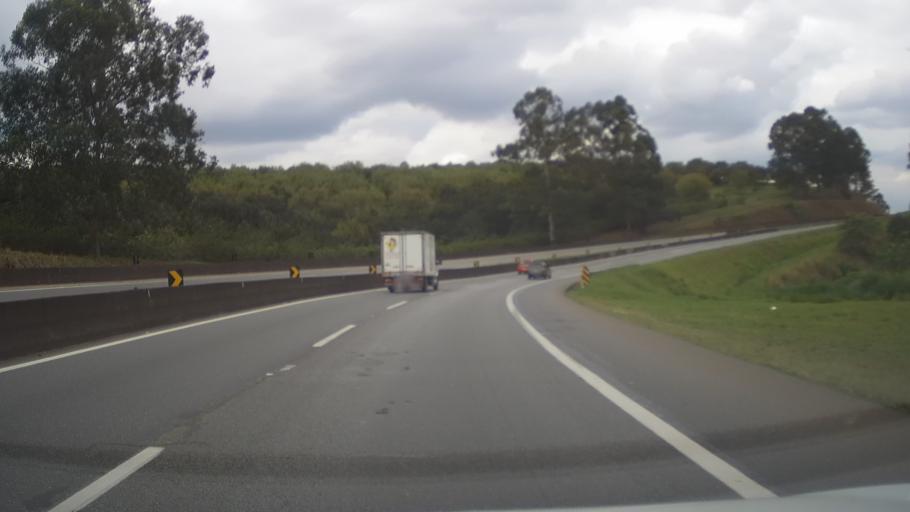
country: BR
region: Minas Gerais
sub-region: Tres Coracoes
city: Tres Coracoes
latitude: -21.5017
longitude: -45.2149
